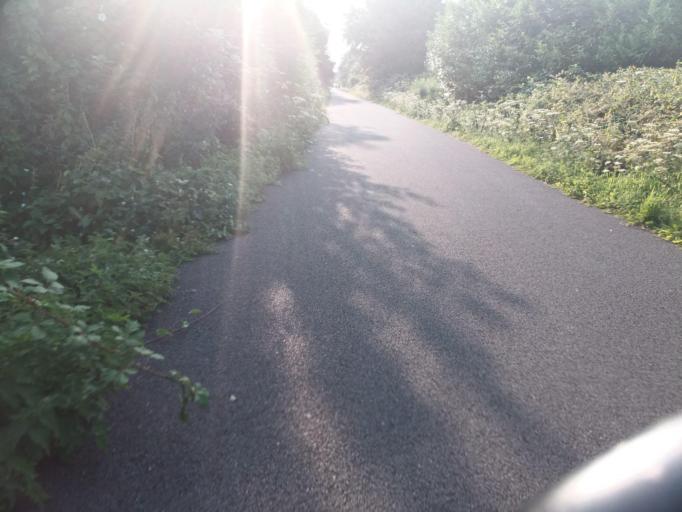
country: GB
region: Northern Ireland
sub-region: Castlereagh District
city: Castlereagh
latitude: 54.5911
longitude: -5.8441
